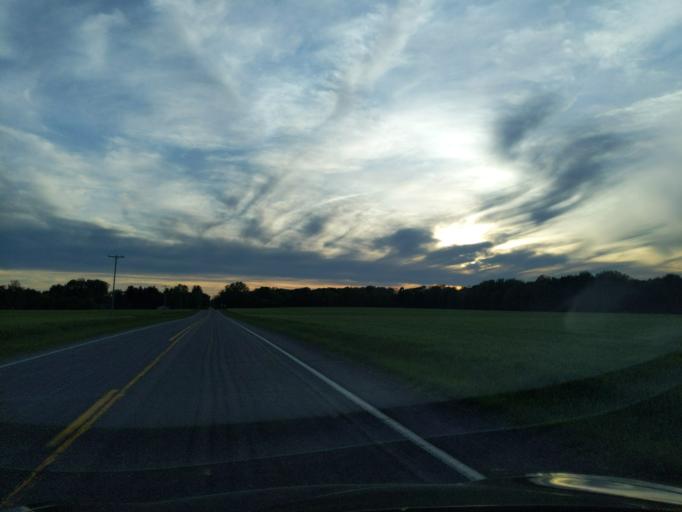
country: US
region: Michigan
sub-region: Ingham County
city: Williamston
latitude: 42.6009
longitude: -84.3223
